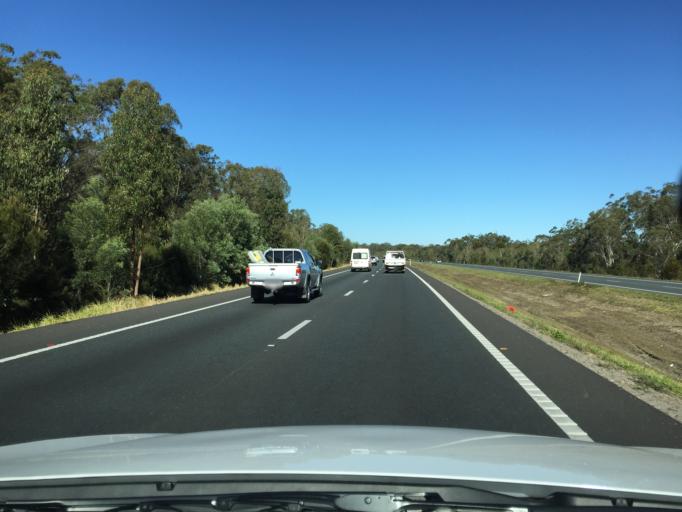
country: AU
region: Queensland
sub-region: Sunshine Coast
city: Little Mountain
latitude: -26.8646
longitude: 153.0142
